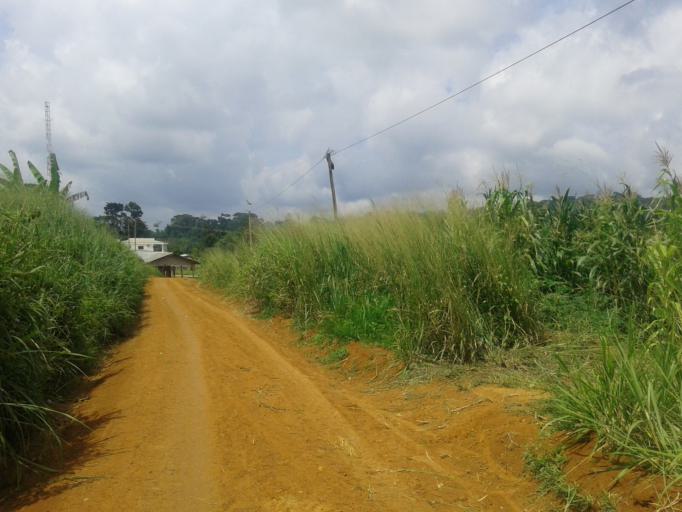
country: CM
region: South Province
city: Mvangue
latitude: 2.9418
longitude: 11.4001
